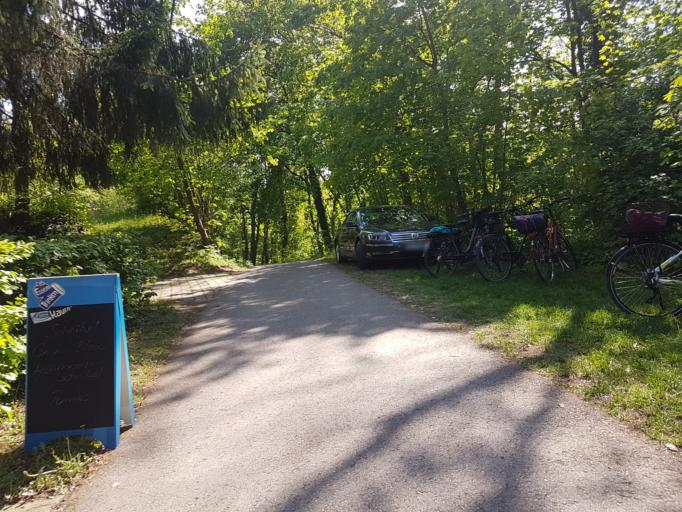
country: DE
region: Baden-Wuerttemberg
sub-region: Regierungsbezirk Stuttgart
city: Besigheim
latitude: 48.9792
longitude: 9.1506
